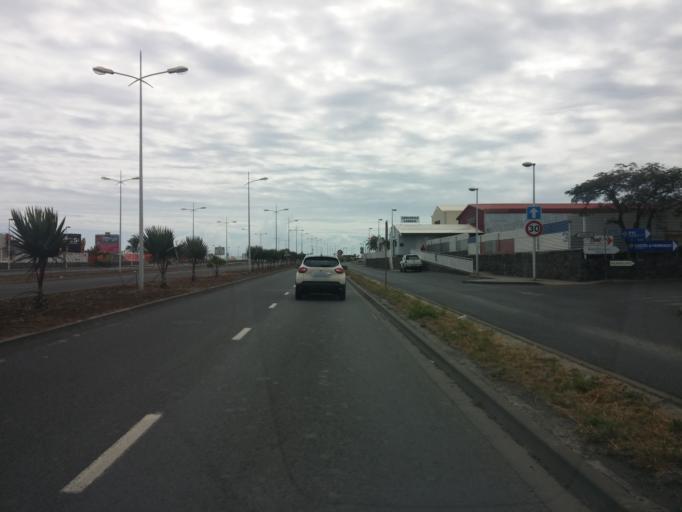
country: RE
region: Reunion
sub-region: Reunion
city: Le Port
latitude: -20.9637
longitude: 55.2944
